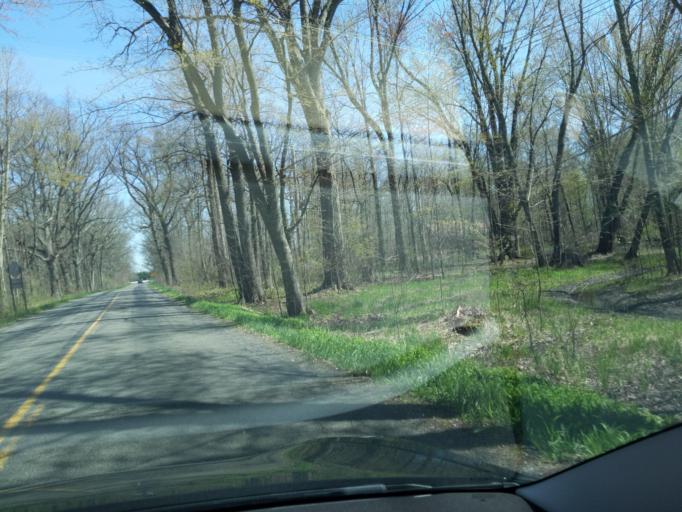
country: US
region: Michigan
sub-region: Ingham County
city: Stockbridge
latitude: 42.4909
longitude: -84.1940
